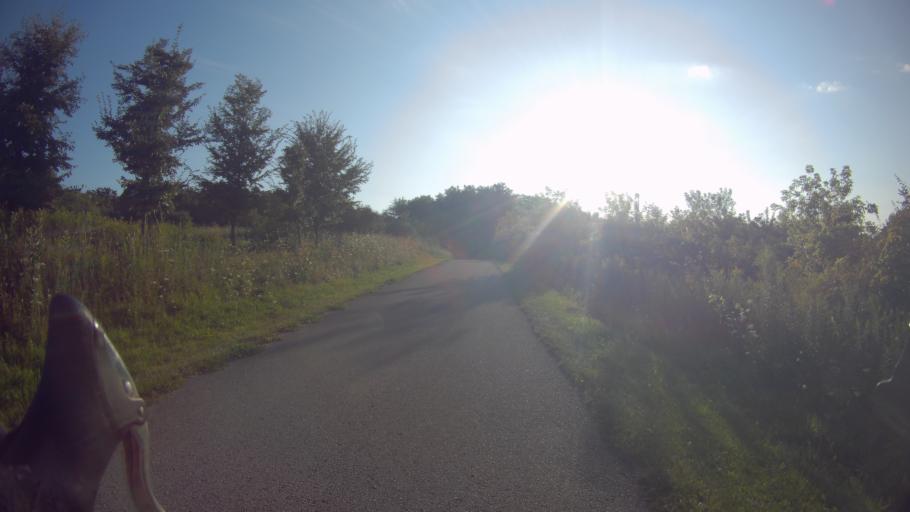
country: US
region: Wisconsin
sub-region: Dane County
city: Madison
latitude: 43.0101
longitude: -89.4145
